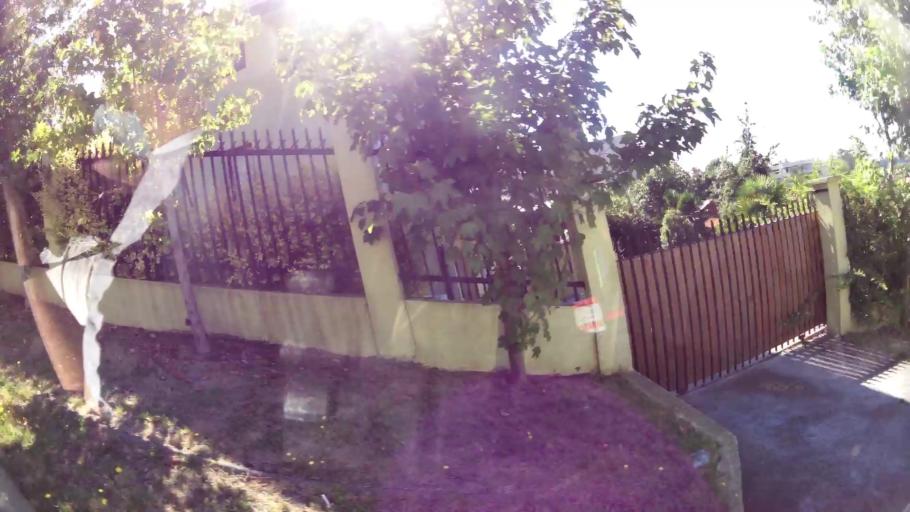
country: CL
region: Biobio
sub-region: Provincia de Concepcion
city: Concepcion
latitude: -36.7940
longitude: -73.0589
